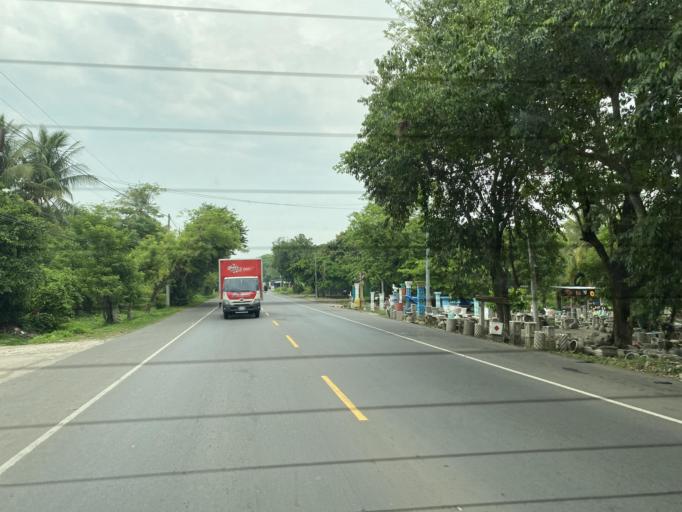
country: SV
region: Usulutan
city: Concepcion Batres
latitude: 13.3453
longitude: -88.3613
